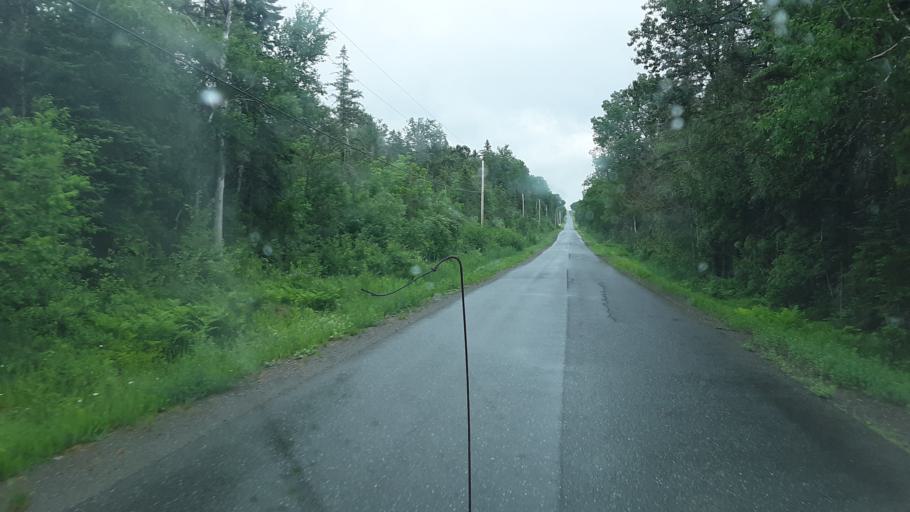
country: US
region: Maine
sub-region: Aroostook County
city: Presque Isle
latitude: 46.6815
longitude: -68.2031
